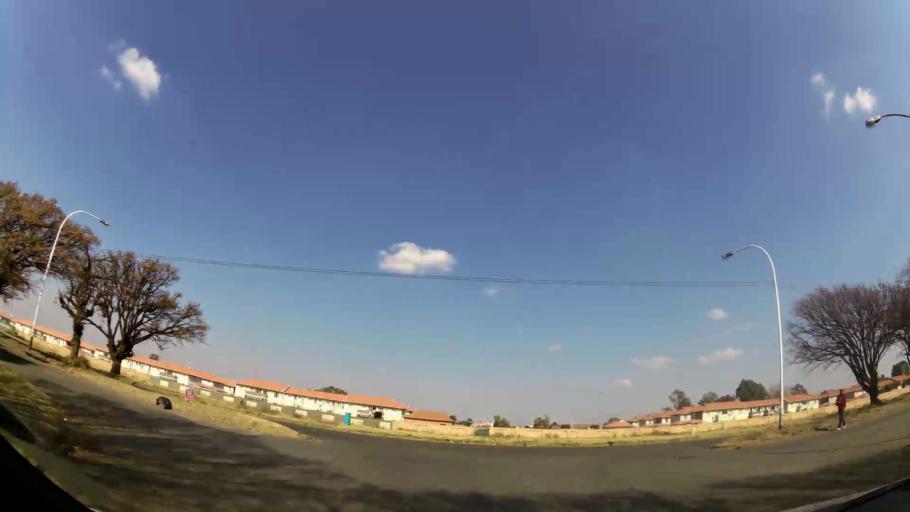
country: ZA
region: Gauteng
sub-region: Ekurhuleni Metropolitan Municipality
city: Boksburg
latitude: -26.2046
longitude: 28.2375
